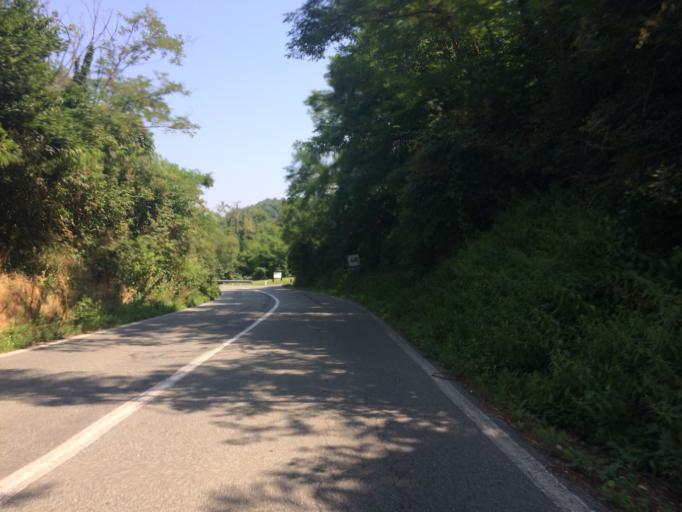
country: IT
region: Piedmont
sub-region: Provincia di Alessandria
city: Castelletto d'Erro
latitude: 44.6162
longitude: 8.4142
